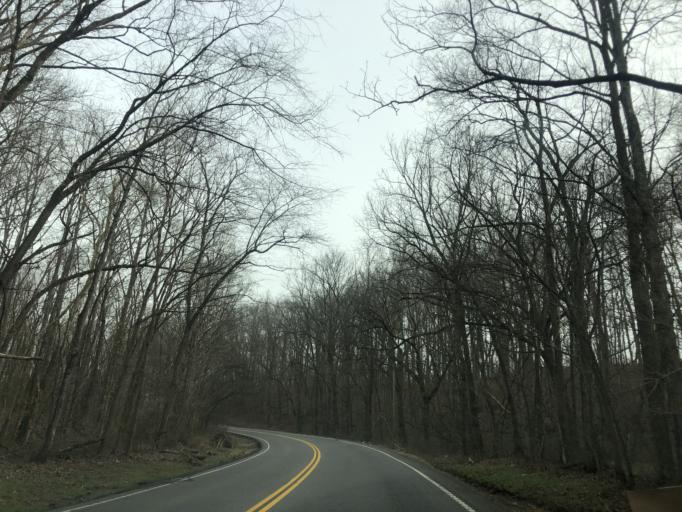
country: US
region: Tennessee
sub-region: Sumner County
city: White House
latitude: 36.5121
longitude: -86.6144
